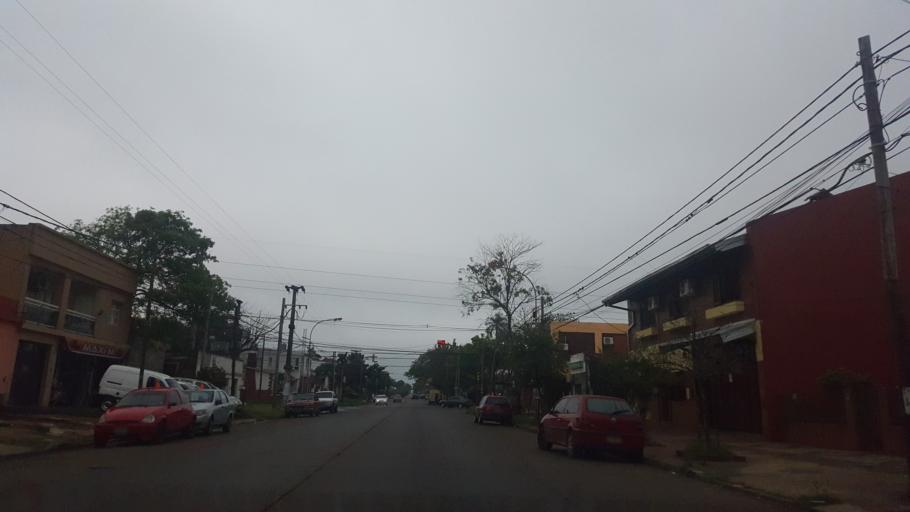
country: AR
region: Misiones
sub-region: Departamento de Capital
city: Posadas
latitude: -27.3694
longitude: -55.9122
